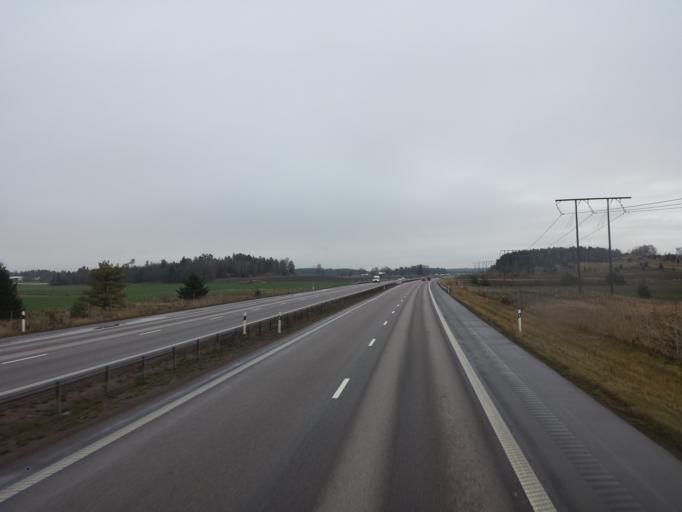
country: SE
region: OEstergoetland
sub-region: Linkopings Kommun
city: Linghem
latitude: 58.4710
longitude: 15.8179
